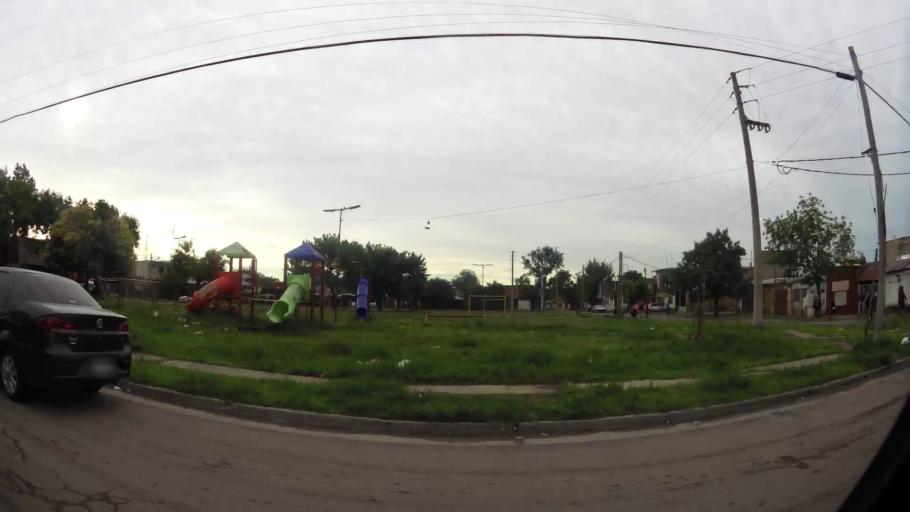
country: AR
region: Buenos Aires
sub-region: Partido de Lanus
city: Lanus
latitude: -34.7266
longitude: -58.3510
